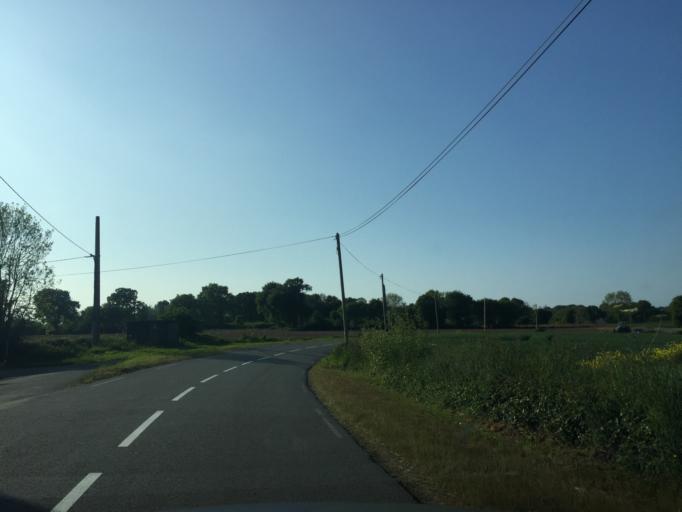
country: FR
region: Brittany
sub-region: Departement des Cotes-d'Armor
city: Saint-Cast-le-Guildo
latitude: 48.6039
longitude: -2.2533
